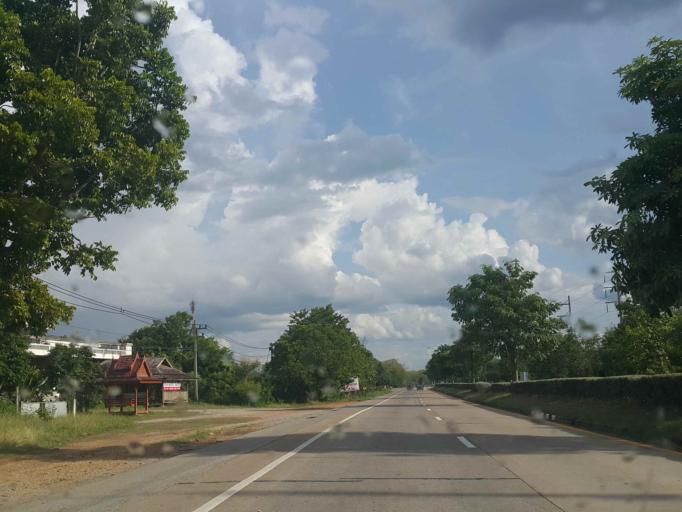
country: TH
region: Phrae
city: Sung Men
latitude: 18.0075
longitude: 100.1051
